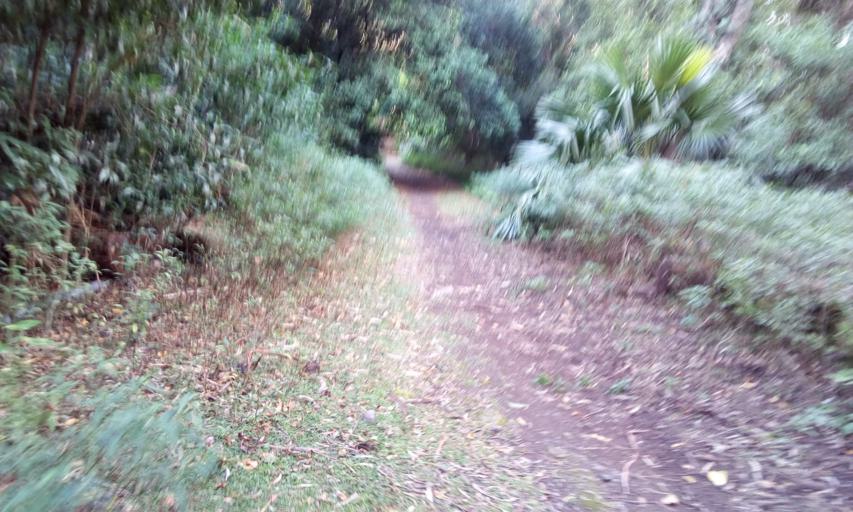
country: AU
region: New South Wales
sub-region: Wollongong
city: Cordeaux Heights
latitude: -34.4447
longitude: 150.8027
